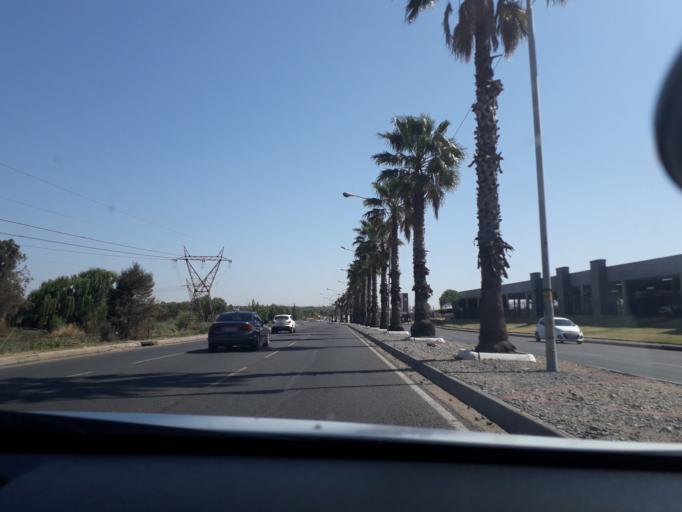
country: ZA
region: Gauteng
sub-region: City of Johannesburg Metropolitan Municipality
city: Modderfontein
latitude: -26.1036
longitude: 28.2212
